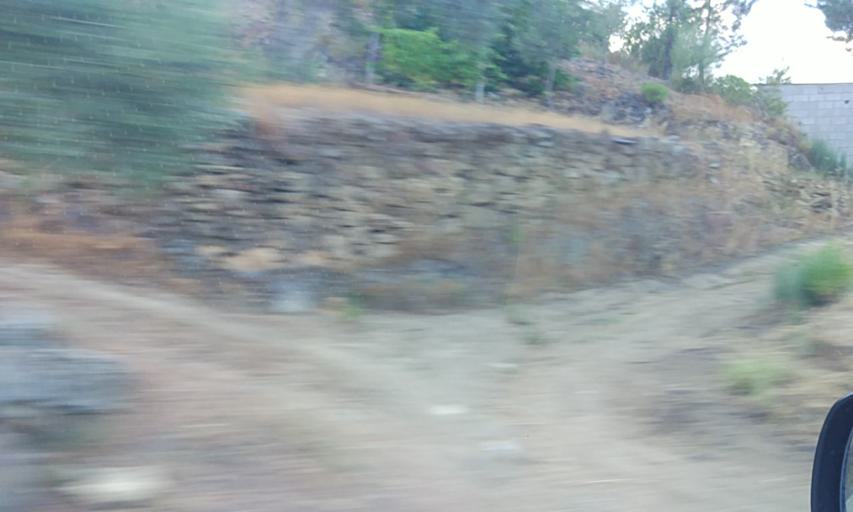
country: PT
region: Viseu
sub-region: Sao Joao da Pesqueira
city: Sao Joao da Pesqueira
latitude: 41.2380
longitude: -7.4310
